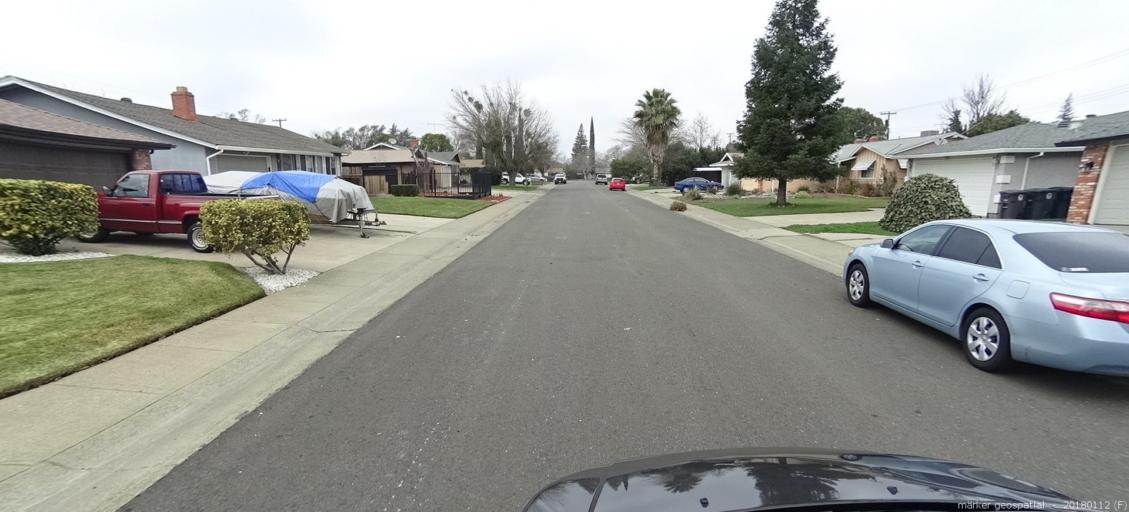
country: US
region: California
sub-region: Sacramento County
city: Rancho Cordova
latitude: 38.6088
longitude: -121.2847
